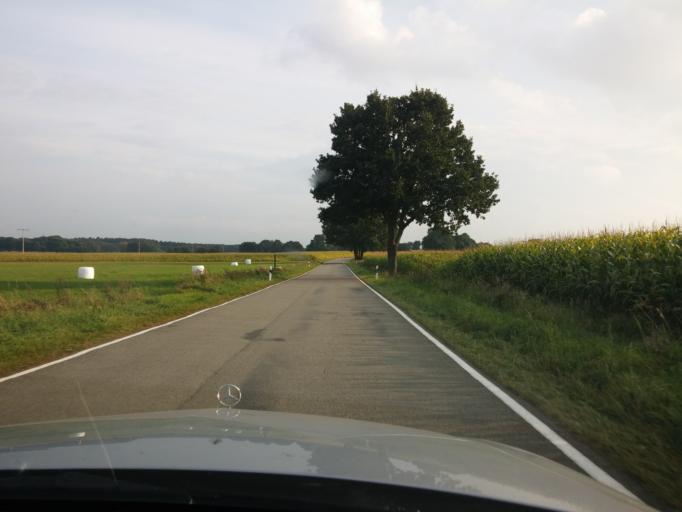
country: DE
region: Brandenburg
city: Putlitz
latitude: 53.2984
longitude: 12.0483
